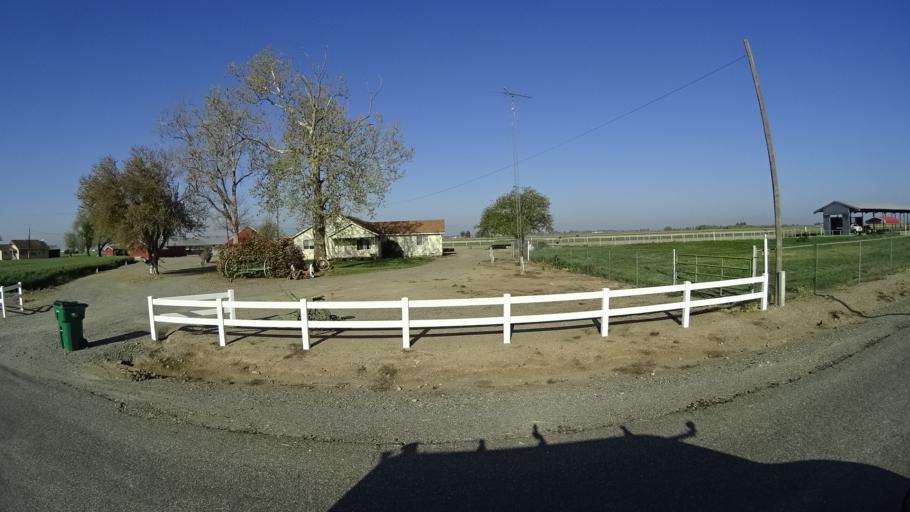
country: US
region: California
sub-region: Glenn County
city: Willows
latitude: 39.5324
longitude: -122.1215
